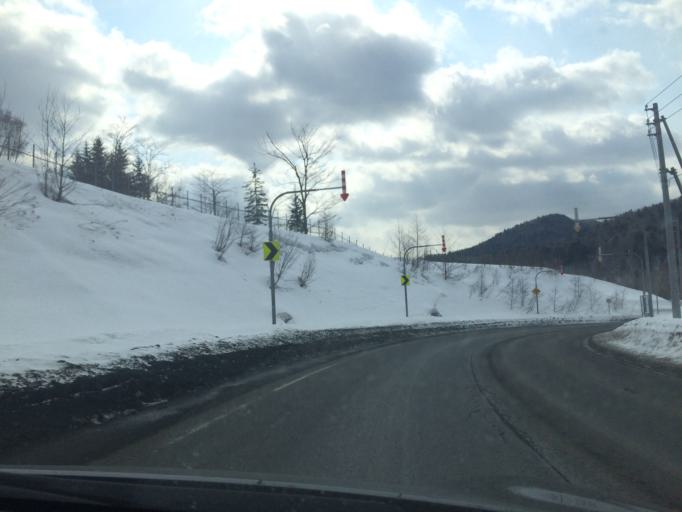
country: JP
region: Hokkaido
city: Shimo-furano
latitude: 42.9781
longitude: 142.4126
